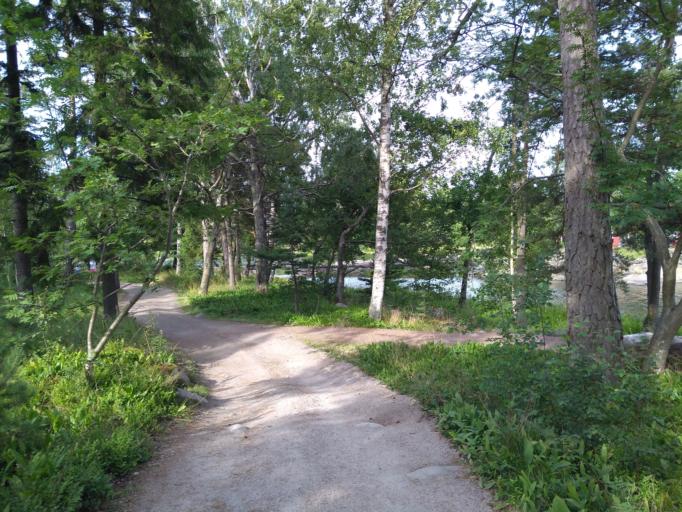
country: FI
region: Uusimaa
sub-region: Helsinki
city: Helsinki
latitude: 60.1381
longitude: 24.9179
